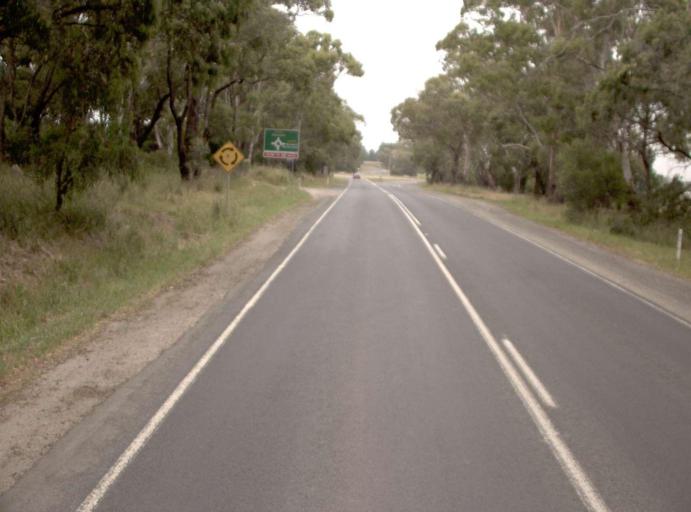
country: AU
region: Victoria
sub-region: Latrobe
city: Traralgon
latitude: -38.2535
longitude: 146.4919
